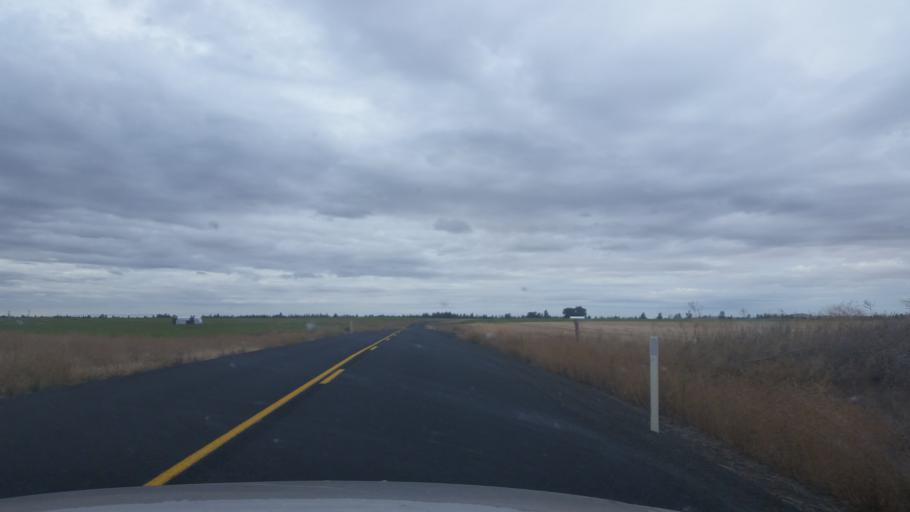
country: US
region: Washington
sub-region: Spokane County
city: Medical Lake
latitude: 47.5144
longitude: -117.7283
